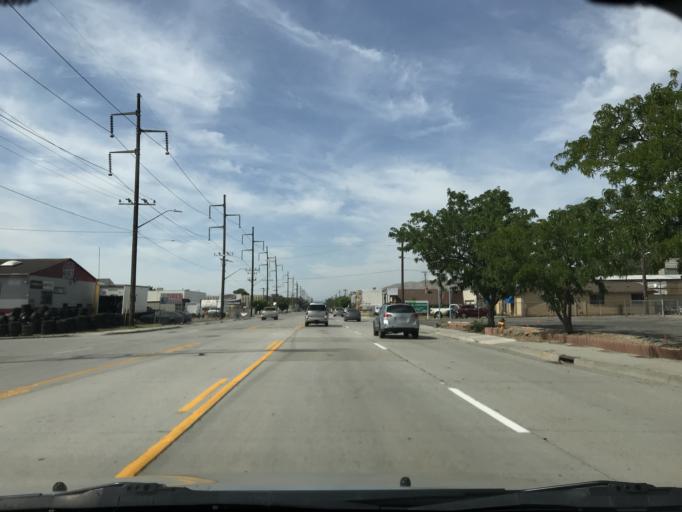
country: US
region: Utah
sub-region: Salt Lake County
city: South Salt Lake
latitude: 40.7285
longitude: -111.9168
